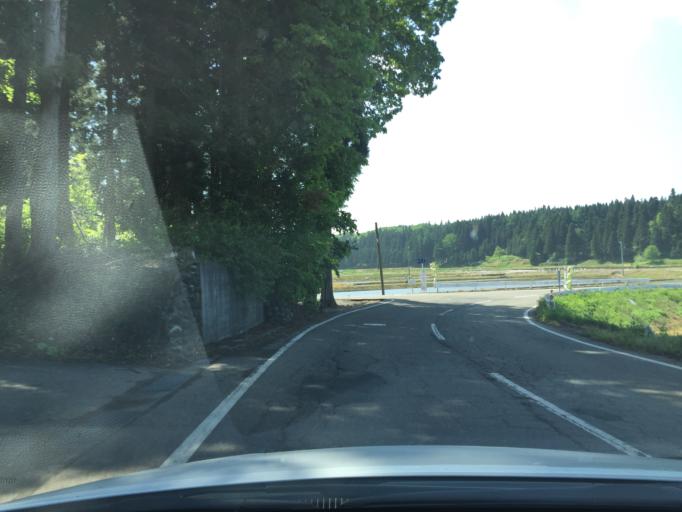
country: JP
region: Niigata
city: Kamo
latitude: 37.5636
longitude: 139.0849
